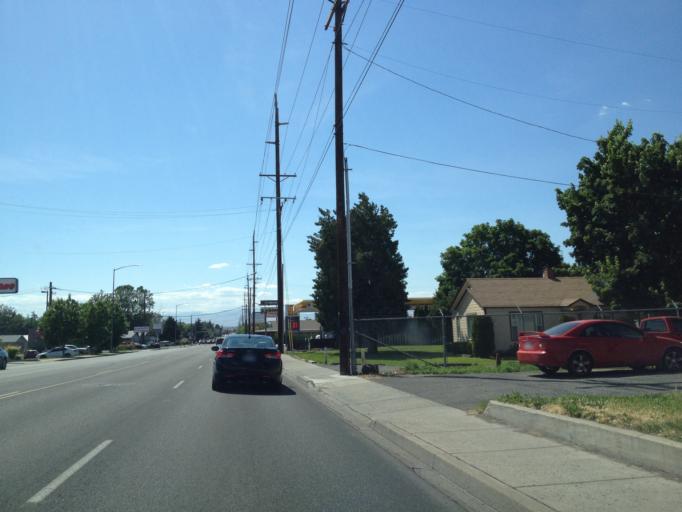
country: US
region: Washington
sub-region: Yakima County
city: West Valley
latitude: 46.5855
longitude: -120.5575
